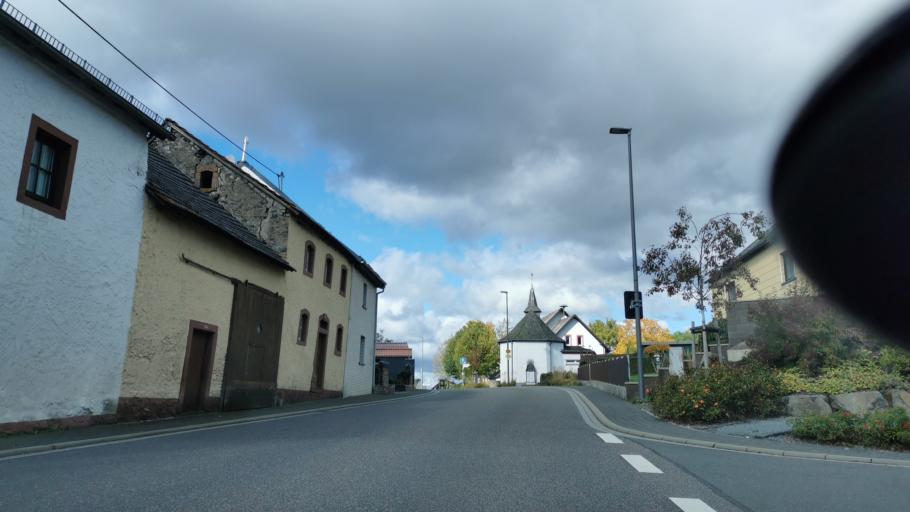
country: DE
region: Rheinland-Pfalz
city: Walsdorf
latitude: 50.2786
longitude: 6.7360
